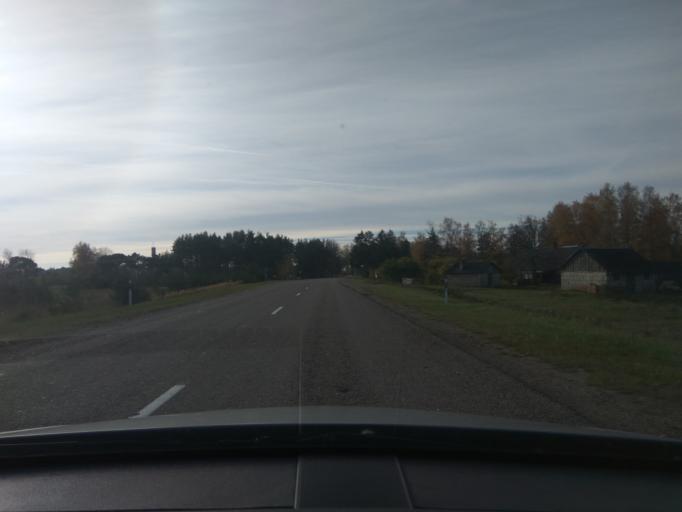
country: LV
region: Alsunga
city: Alsunga
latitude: 57.0084
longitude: 21.3884
